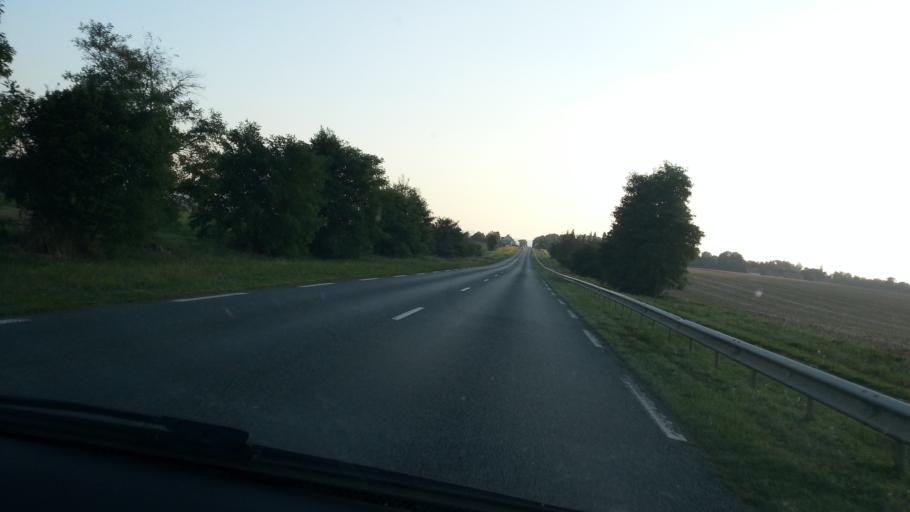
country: FR
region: Picardie
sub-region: Departement de l'Oise
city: Grandfresnoy
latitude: 49.3918
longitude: 2.6225
